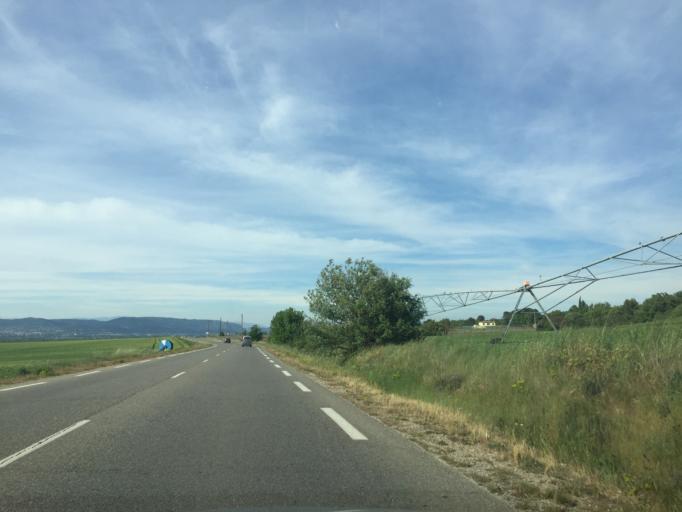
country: FR
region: Provence-Alpes-Cote d'Azur
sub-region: Departement du Var
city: Vinon-sur-Verdon
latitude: 43.7459
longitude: 5.8029
